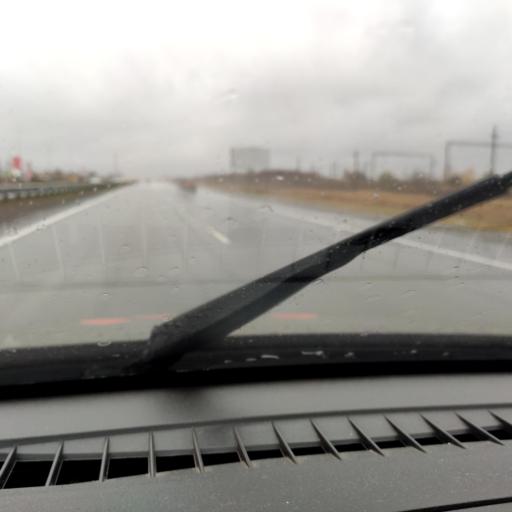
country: RU
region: Samara
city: Tol'yatti
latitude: 53.5716
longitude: 49.3855
